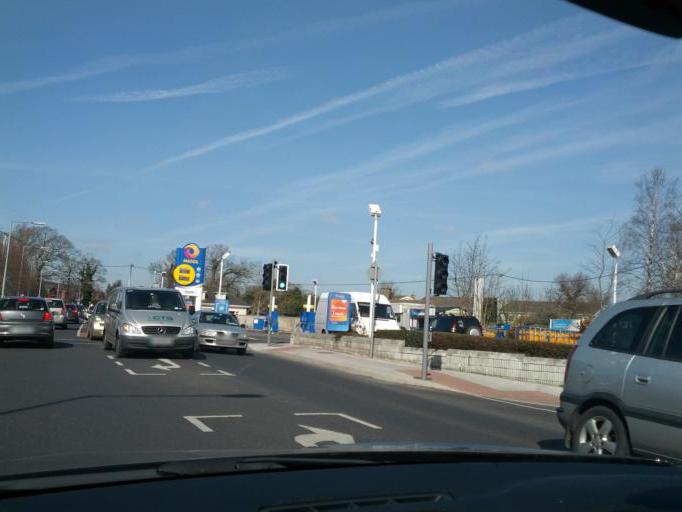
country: IE
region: Leinster
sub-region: Kildare
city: Celbridge
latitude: 53.3507
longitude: -6.5451
